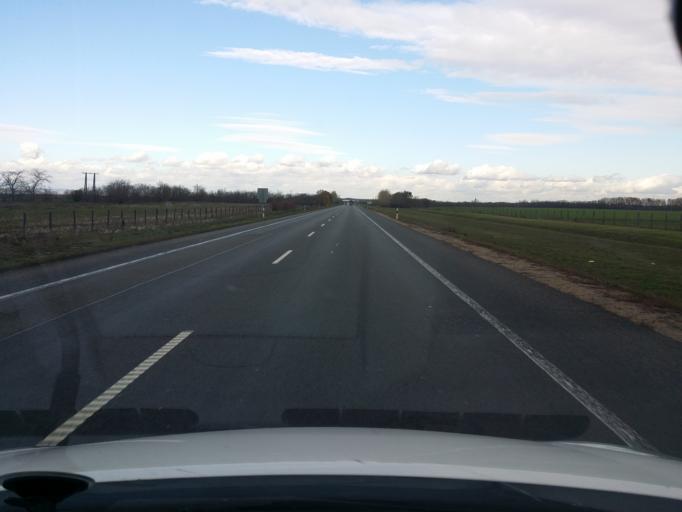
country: HU
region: Gyor-Moson-Sopron
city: Rajka
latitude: 47.9679
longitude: 17.1752
